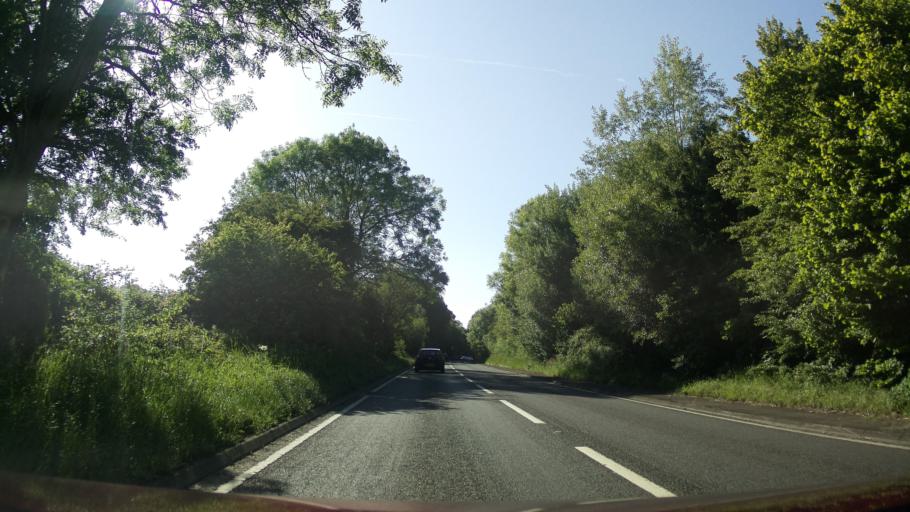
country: GB
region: England
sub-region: Somerset
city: Yeovil
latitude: 50.9409
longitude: -2.6783
